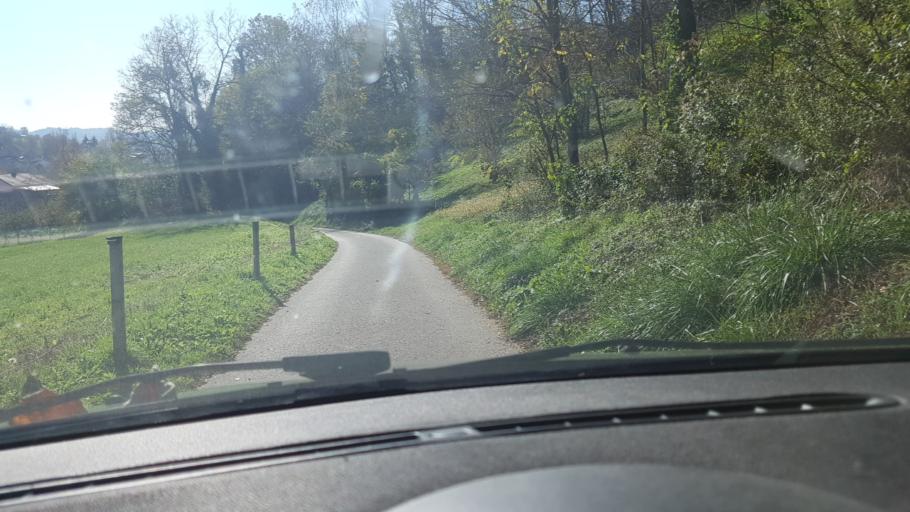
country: HR
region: Krapinsko-Zagorska
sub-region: Grad Krapina
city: Krapina
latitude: 46.1548
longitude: 15.8815
